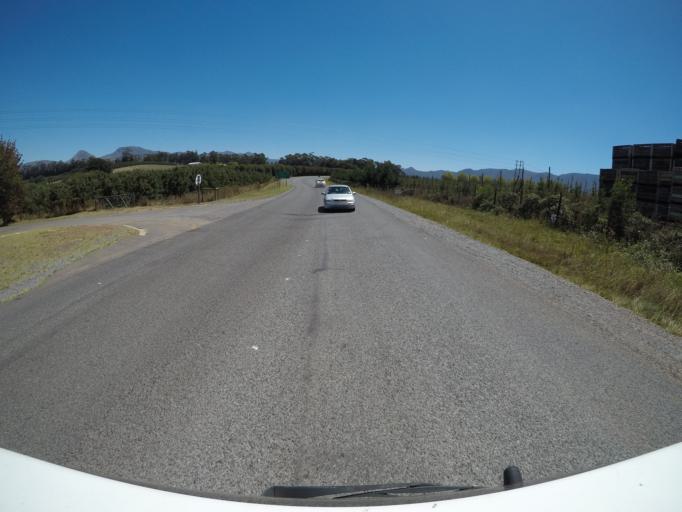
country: ZA
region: Western Cape
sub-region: Overberg District Municipality
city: Grabouw
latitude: -34.1684
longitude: 19.0362
